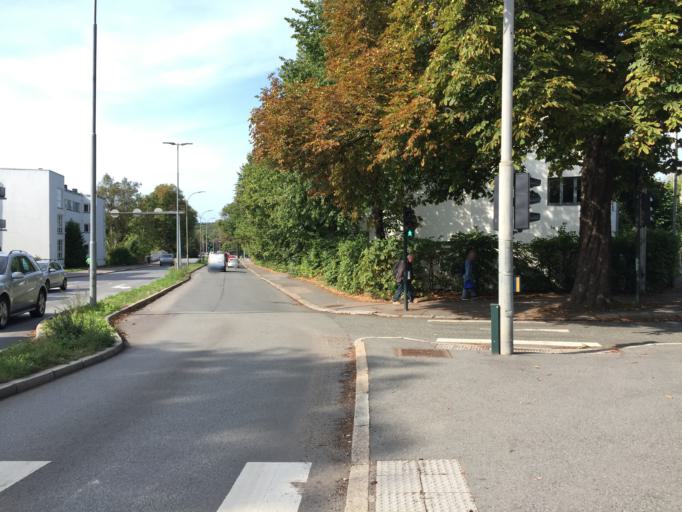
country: NO
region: Oslo
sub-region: Oslo
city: Sjolyststranda
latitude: 59.9193
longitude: 10.6947
